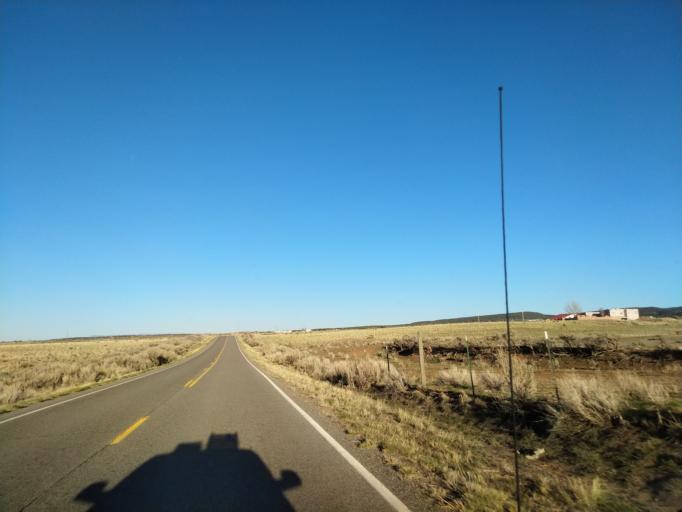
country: US
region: Colorado
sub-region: Mesa County
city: Redlands
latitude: 38.9902
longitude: -108.7564
